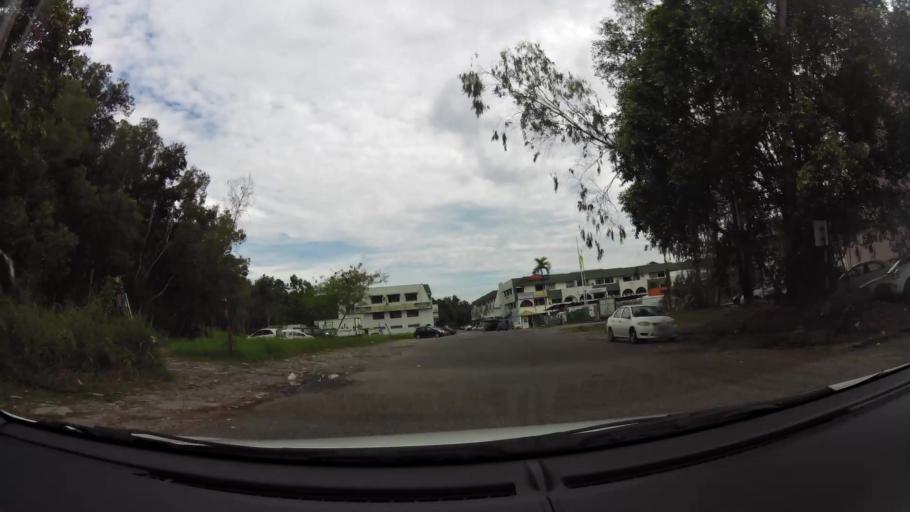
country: BN
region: Brunei and Muara
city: Bandar Seri Begawan
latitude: 4.8794
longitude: 114.8939
